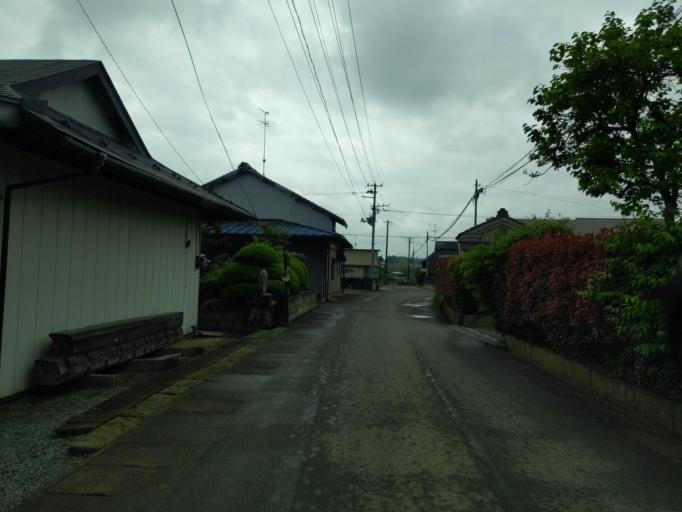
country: JP
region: Fukushima
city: Koriyama
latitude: 37.3598
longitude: 140.3195
